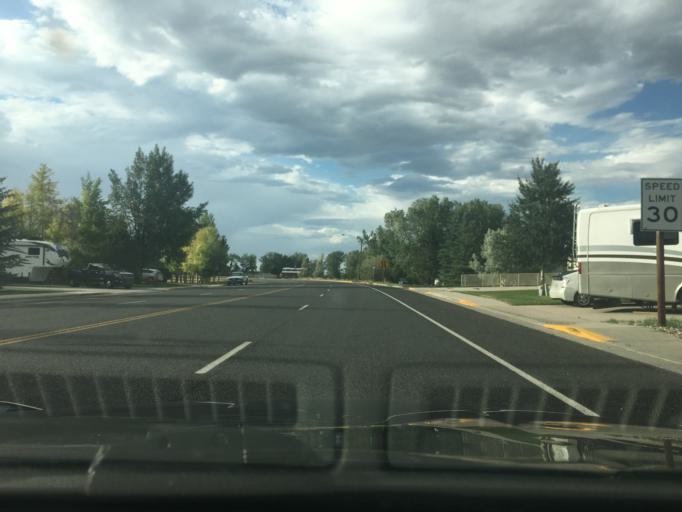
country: US
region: Wyoming
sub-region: Albany County
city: Laramie
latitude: 41.3123
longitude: -105.6292
